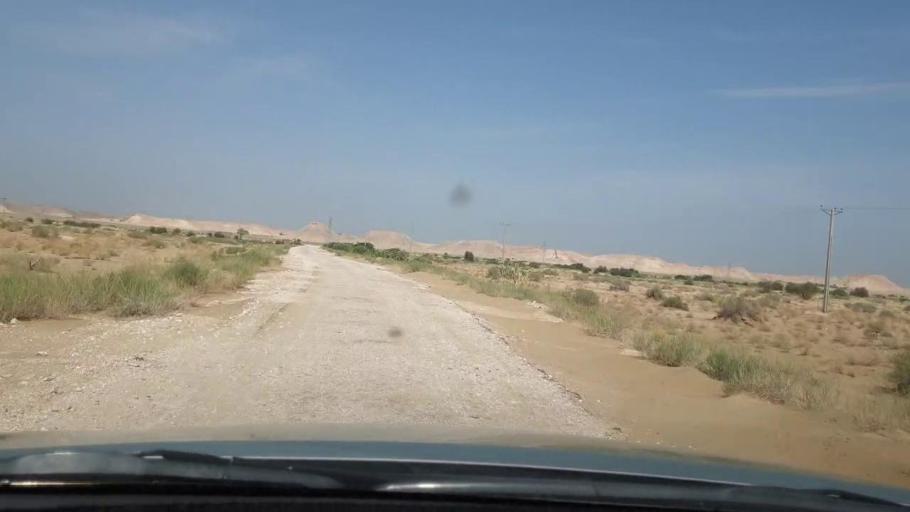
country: PK
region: Sindh
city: Kot Diji
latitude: 27.3279
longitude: 68.7961
